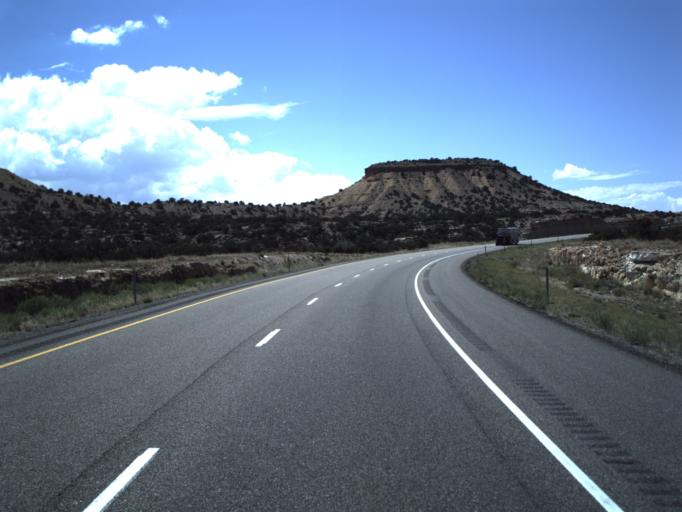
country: US
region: Utah
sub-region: Emery County
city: Castle Dale
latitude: 38.9139
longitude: -110.5062
